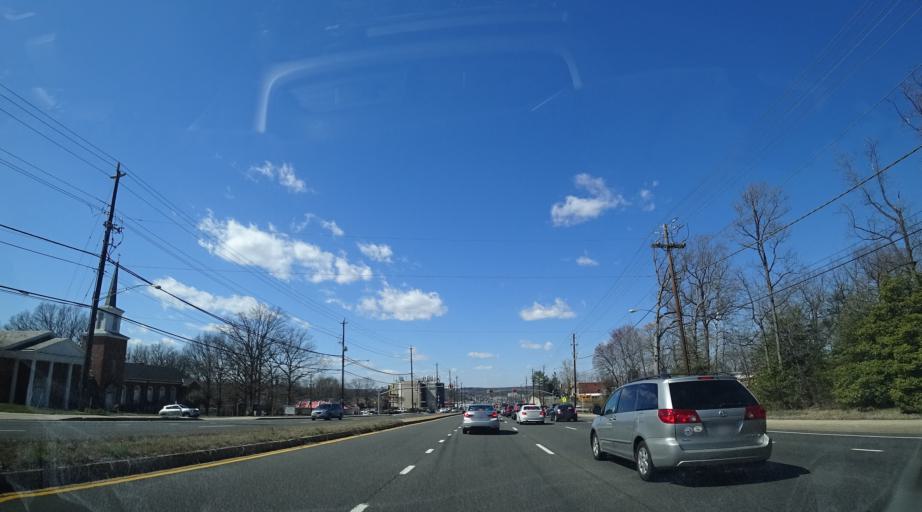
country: US
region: Maryland
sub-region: Prince George's County
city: Berwyn Heights
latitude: 38.9966
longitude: -76.9035
